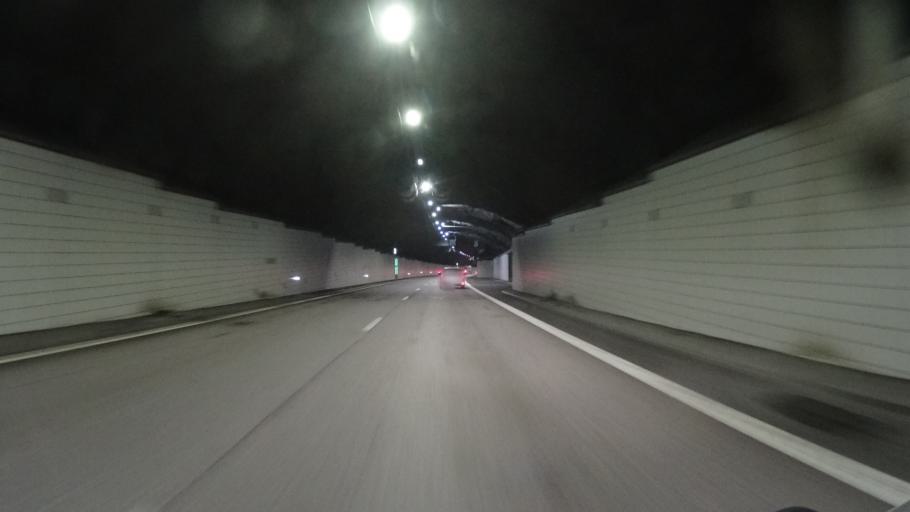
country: SE
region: Vaestra Goetaland
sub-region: Goteborg
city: Majorna
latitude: 57.7098
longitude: 11.8938
